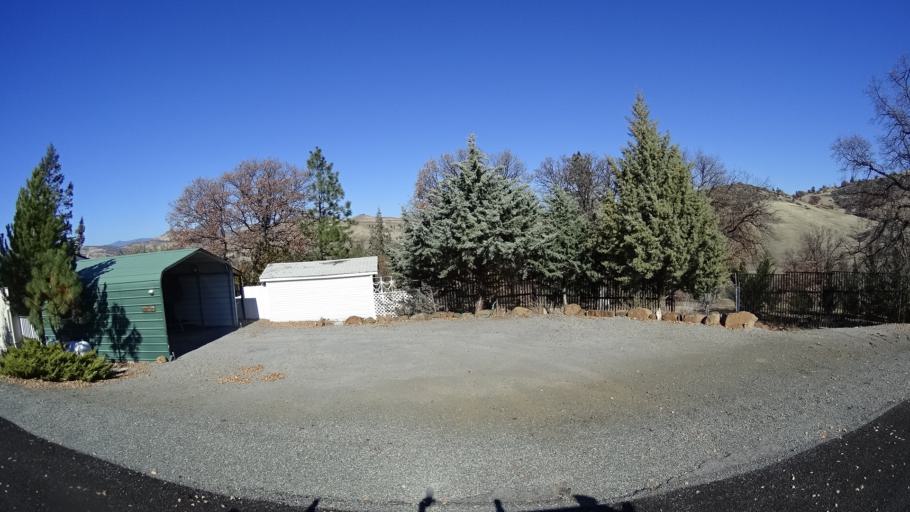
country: US
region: California
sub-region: Siskiyou County
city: Montague
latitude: 41.8864
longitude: -122.4822
